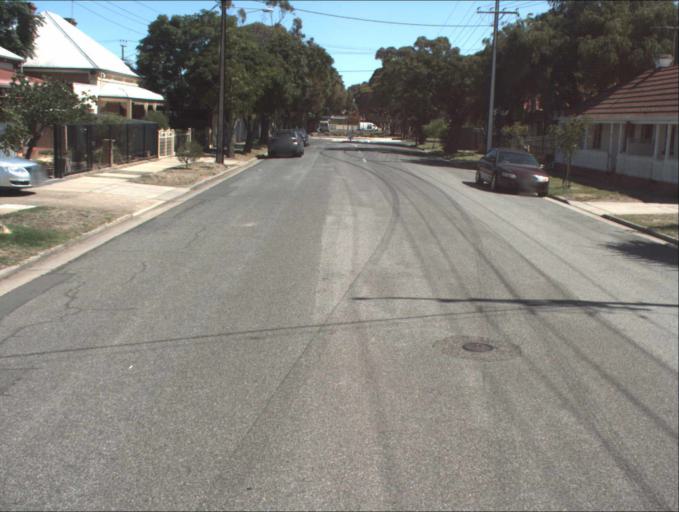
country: AU
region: South Australia
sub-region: Port Adelaide Enfield
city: Alberton
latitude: -34.8592
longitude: 138.5149
